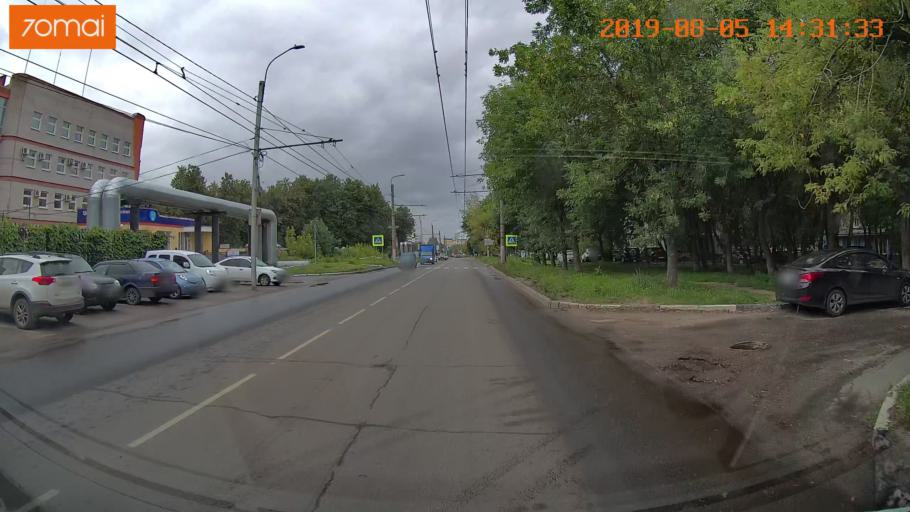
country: RU
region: Ivanovo
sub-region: Gorod Ivanovo
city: Ivanovo
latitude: 56.9875
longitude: 41.0005
